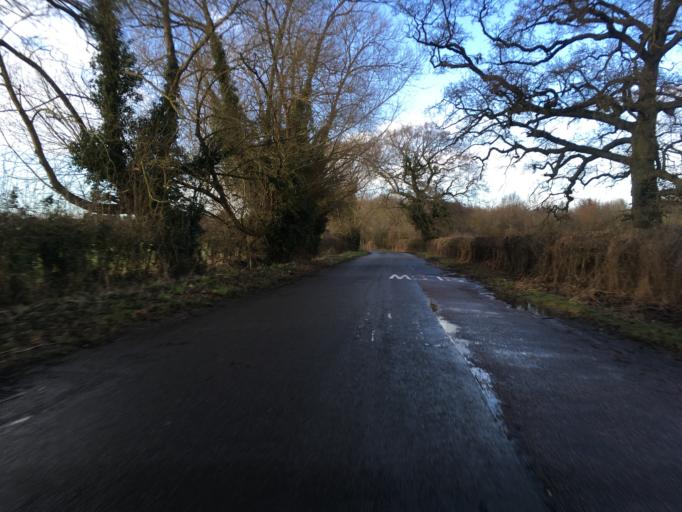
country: GB
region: England
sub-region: Warwickshire
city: Alcester
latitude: 52.2281
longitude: -1.8279
